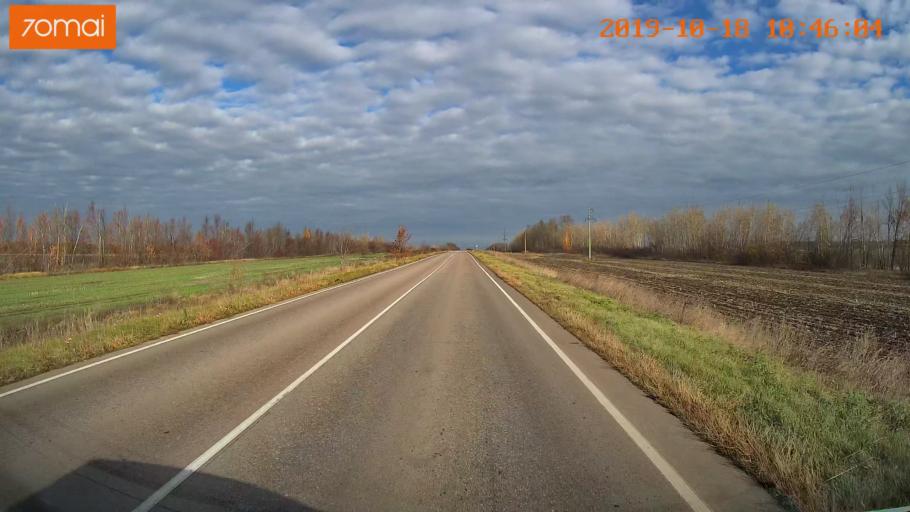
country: RU
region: Tula
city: Yepifan'
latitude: 53.6796
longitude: 38.6917
